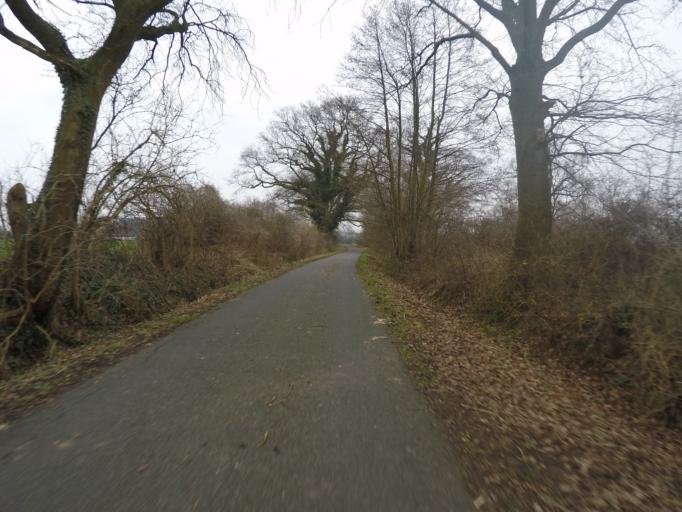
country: DE
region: Schleswig-Holstein
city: Borstel-Hohenraden
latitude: 53.6986
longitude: 9.8292
